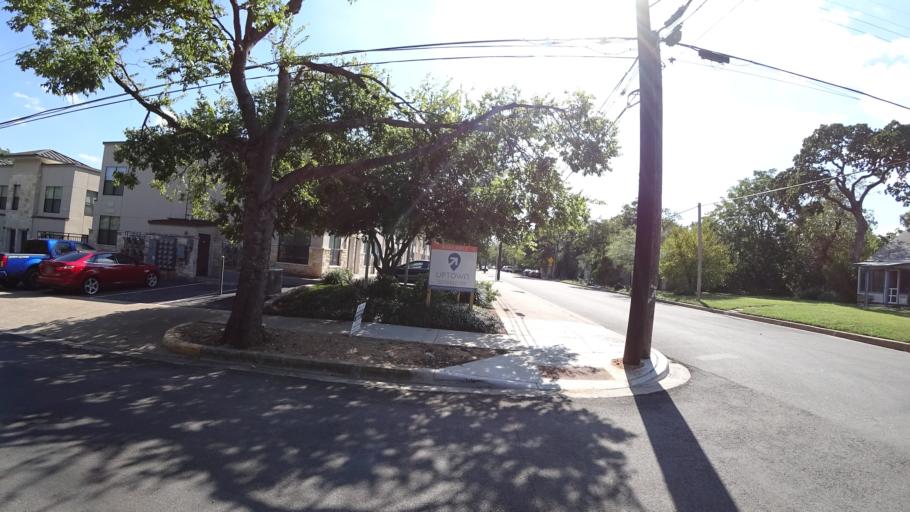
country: US
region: Texas
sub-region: Travis County
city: Austin
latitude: 30.3005
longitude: -97.7434
